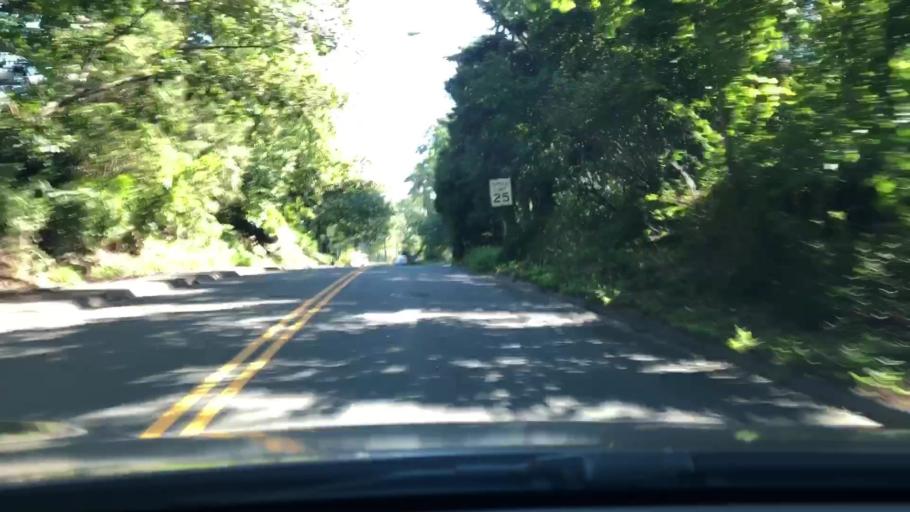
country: US
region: Connecticut
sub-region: Fairfield County
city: Norwalk
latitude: 41.1068
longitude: -73.4437
